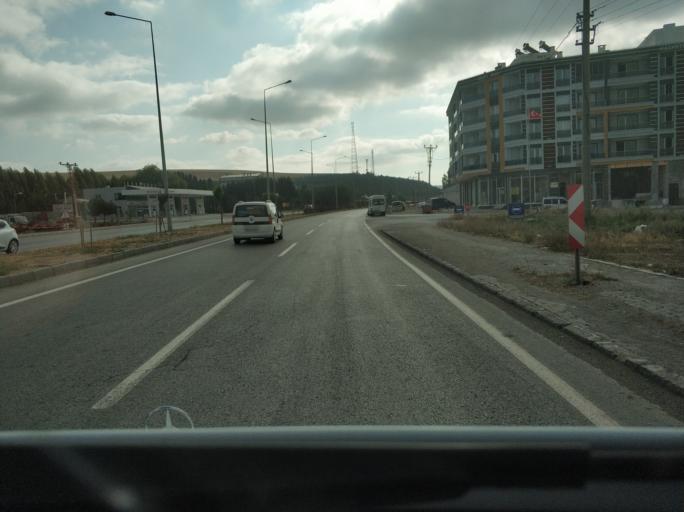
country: TR
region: Sivas
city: Yildizeli
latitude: 39.8720
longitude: 36.6015
